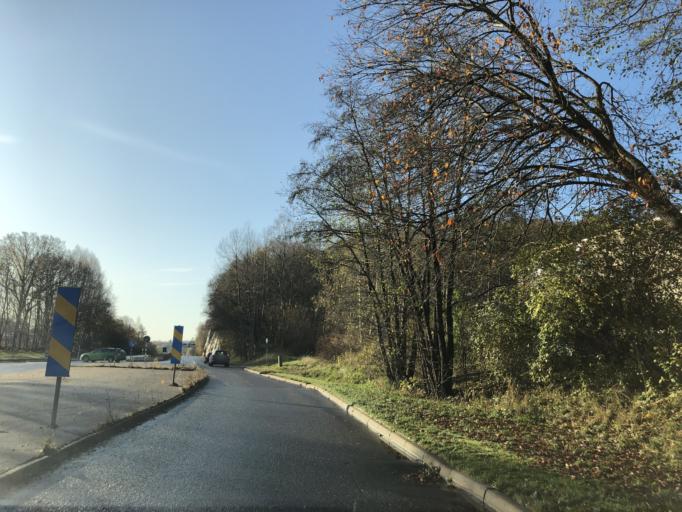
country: SE
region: Vaestra Goetaland
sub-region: Goteborg
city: Gardsten
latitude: 57.8011
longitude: 12.0421
